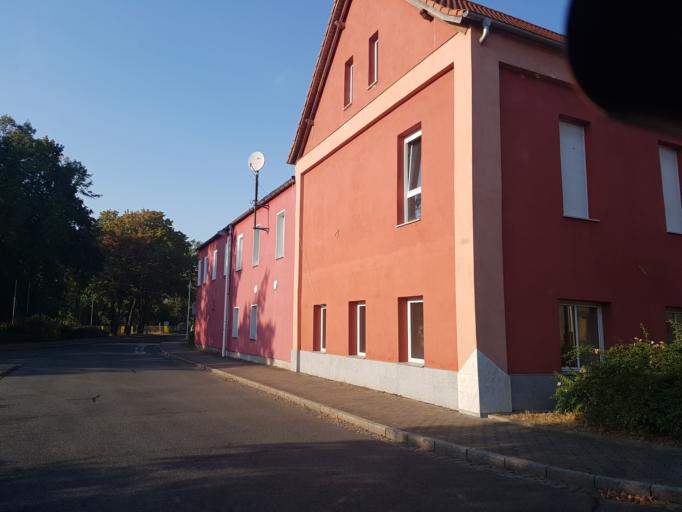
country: DE
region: Saxony
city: Strehla
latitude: 51.3134
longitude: 13.2206
